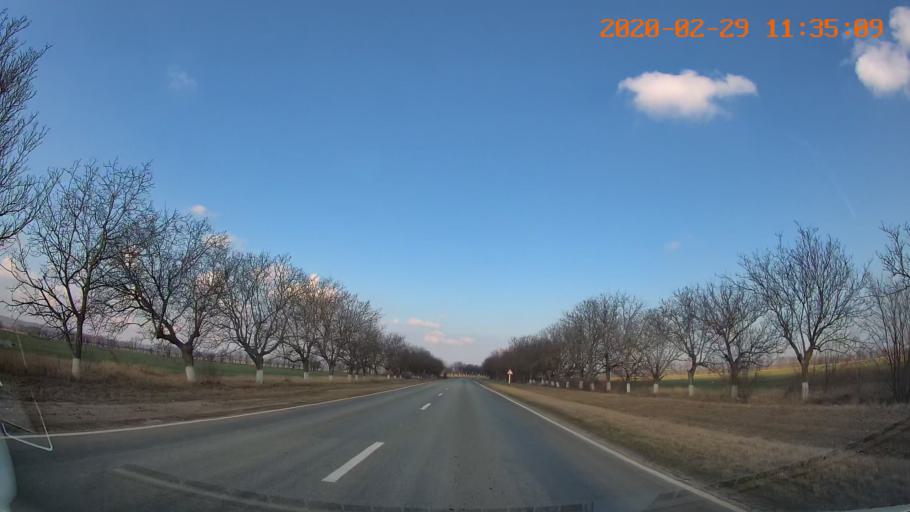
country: MD
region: Rezina
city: Saharna
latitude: 47.5760
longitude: 29.0661
